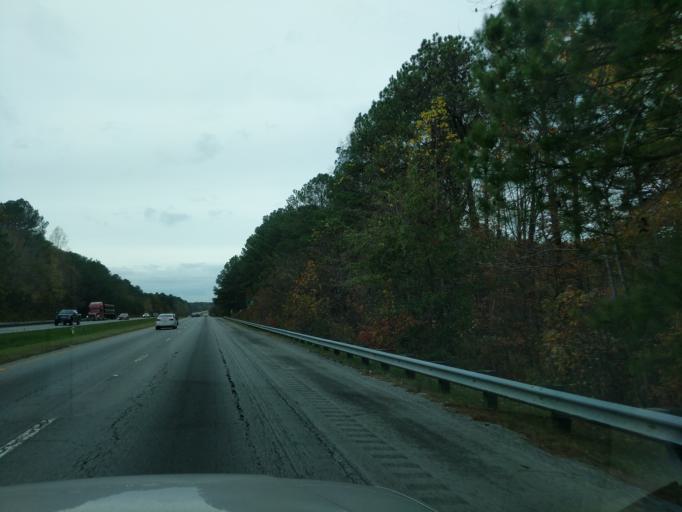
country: US
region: South Carolina
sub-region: Laurens County
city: Joanna
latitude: 34.4316
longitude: -81.7396
